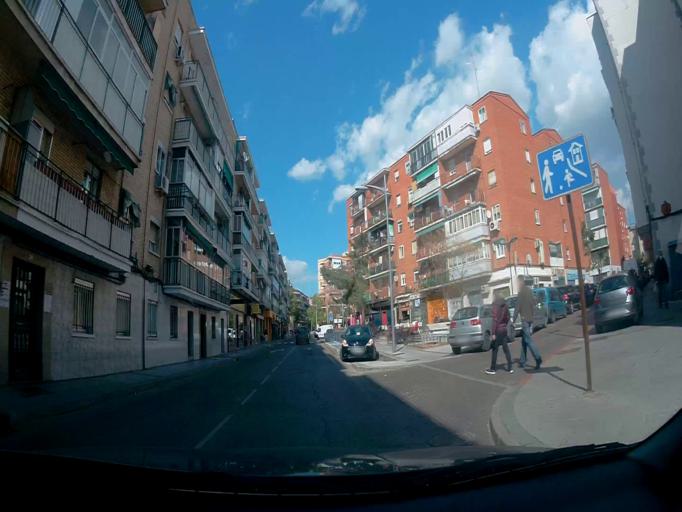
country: ES
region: Madrid
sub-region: Provincia de Madrid
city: Alcorcon
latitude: 40.3480
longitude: -3.8323
